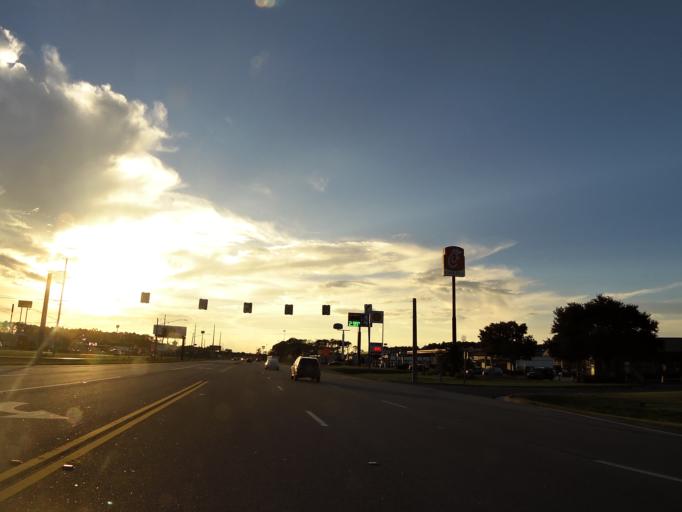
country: US
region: Georgia
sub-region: Camden County
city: Kingsland
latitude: 30.7886
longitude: -81.6523
